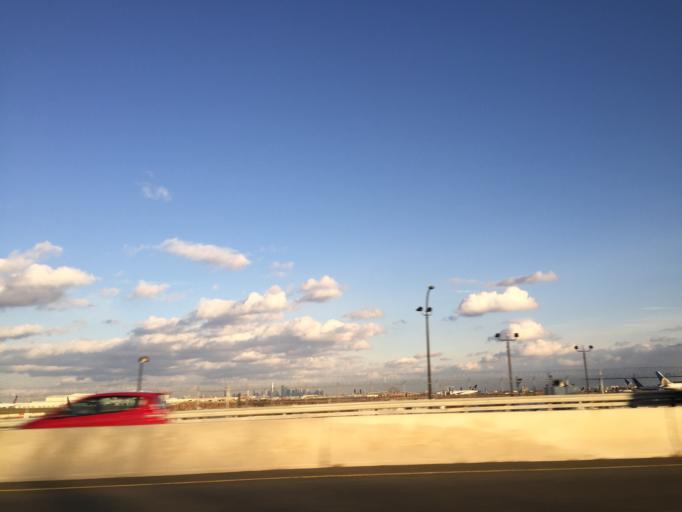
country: US
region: New Jersey
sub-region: Essex County
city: Newark
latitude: 40.7018
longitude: -74.1837
